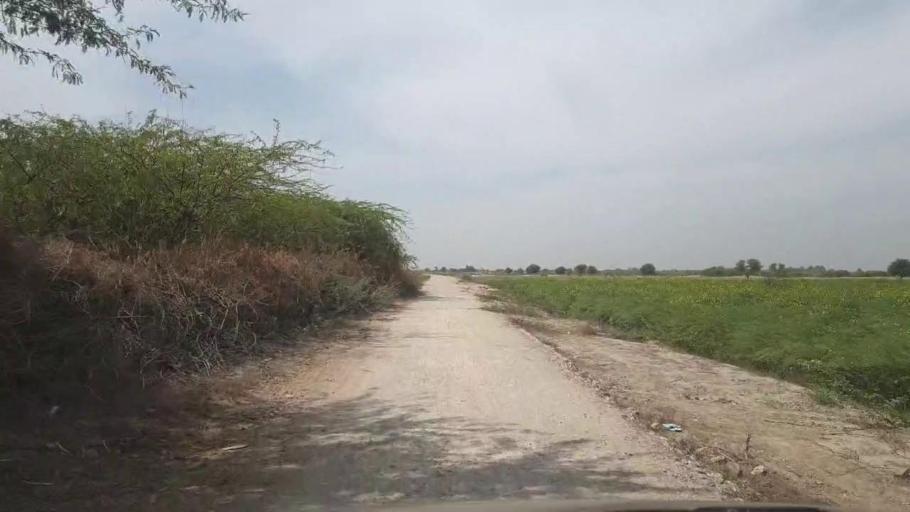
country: PK
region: Sindh
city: Kunri
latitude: 25.2297
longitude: 69.6629
